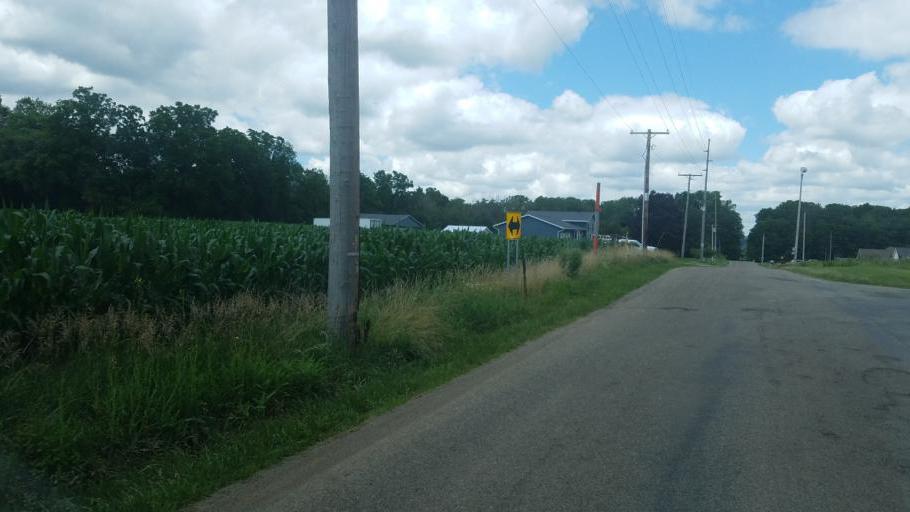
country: US
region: Ohio
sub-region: Richland County
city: Lexington
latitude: 40.6854
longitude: -82.6267
